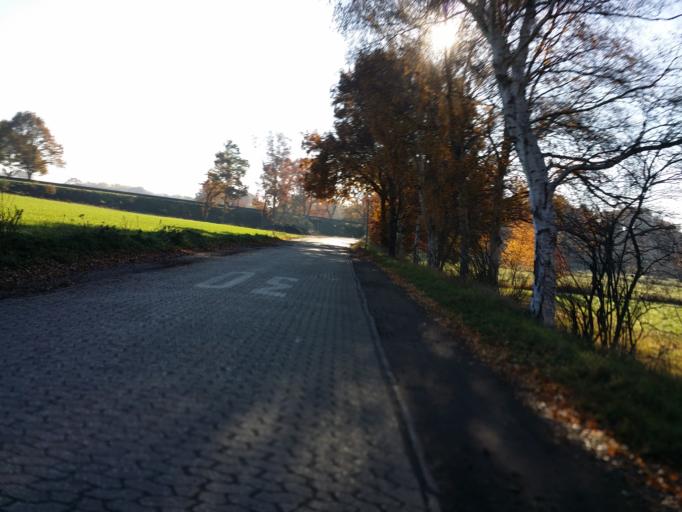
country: DE
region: Lower Saxony
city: Oyten
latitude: 53.0727
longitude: 8.9946
